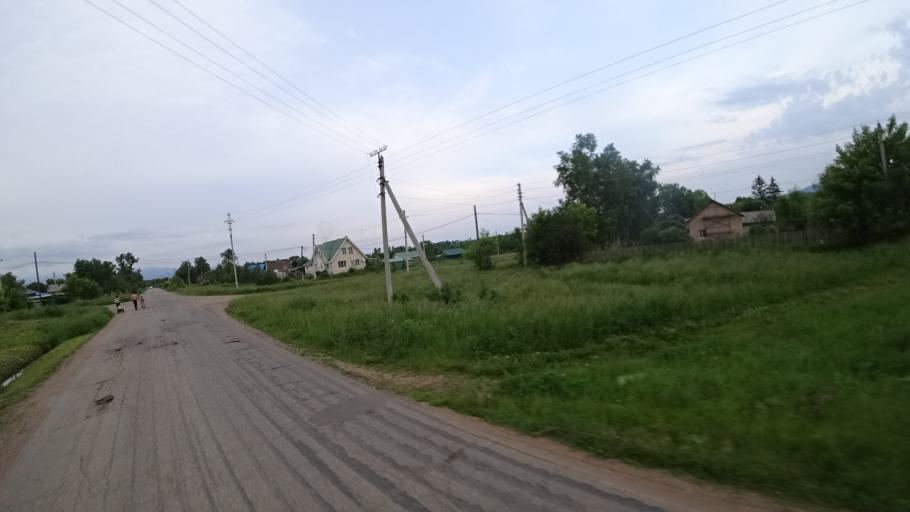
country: RU
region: Primorskiy
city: Novosysoyevka
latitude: 44.2403
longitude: 133.3684
